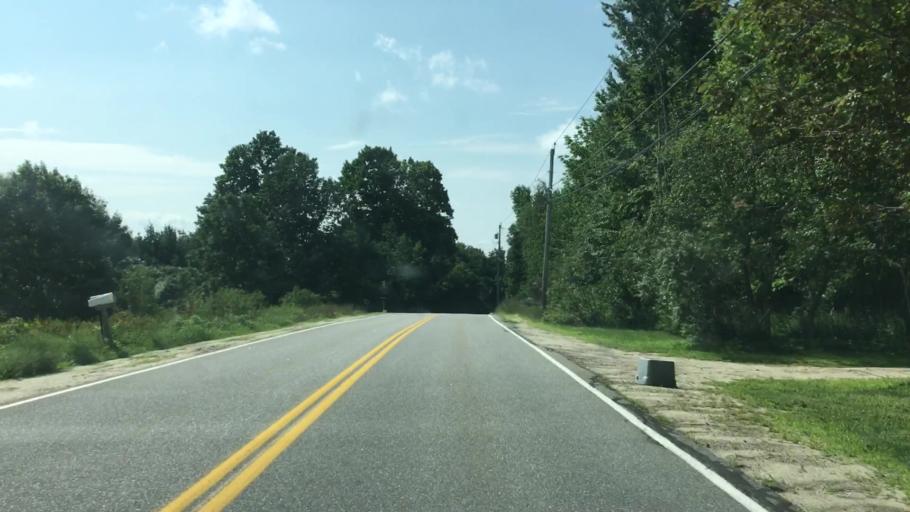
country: US
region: Maine
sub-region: Cumberland County
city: Raymond
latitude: 43.9418
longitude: -70.4383
